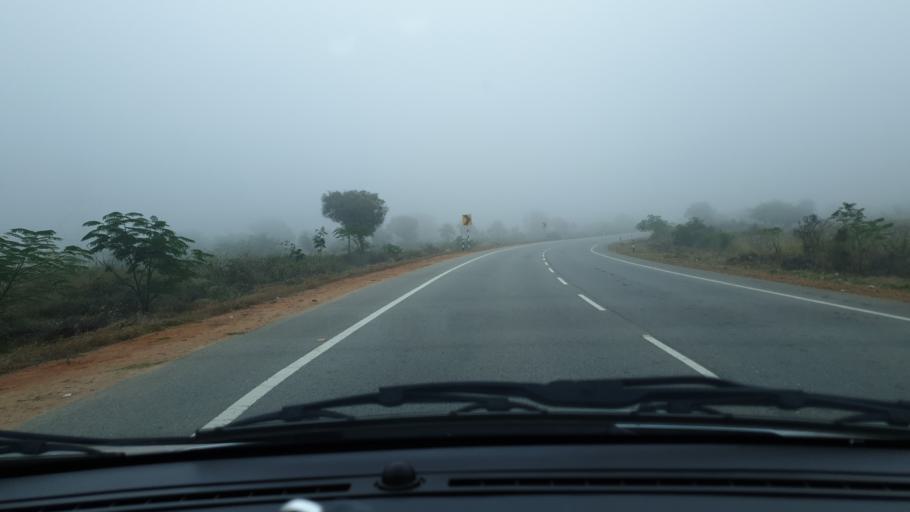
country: IN
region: Telangana
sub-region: Nalgonda
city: Devarkonda
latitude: 16.6229
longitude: 78.6708
